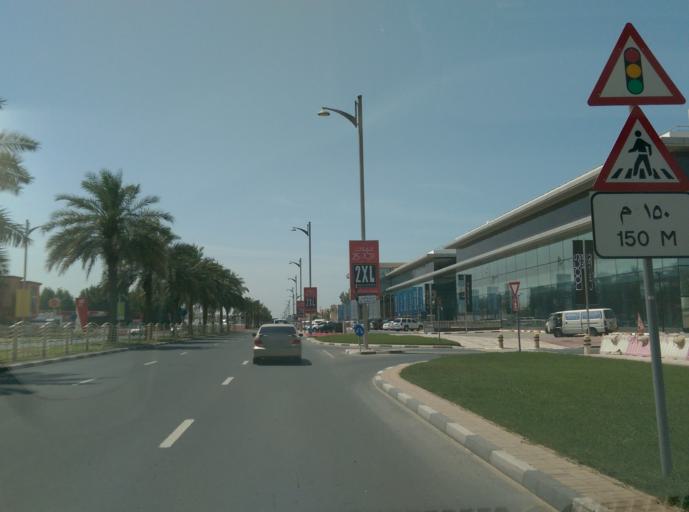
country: AE
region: Dubai
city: Dubai
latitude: 25.1848
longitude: 55.2274
